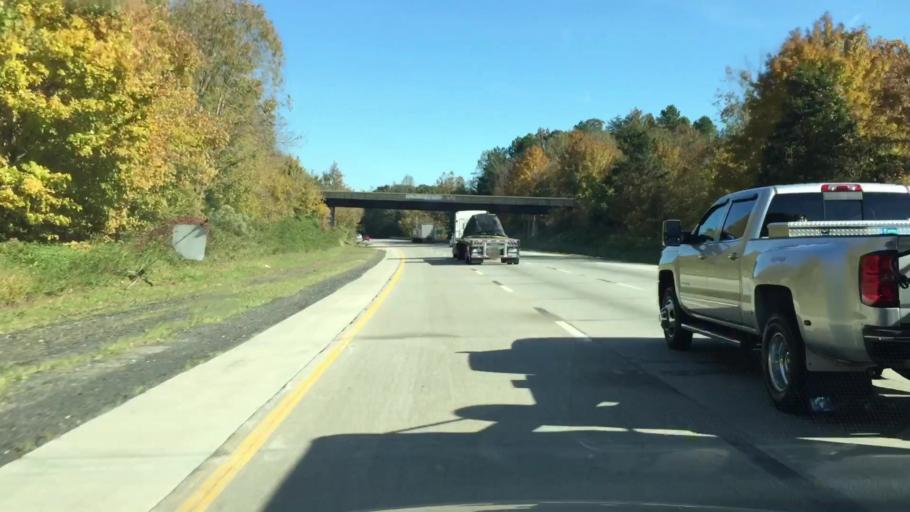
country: US
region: North Carolina
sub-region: Guilford County
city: Jamestown
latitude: 35.9411
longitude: -79.9043
